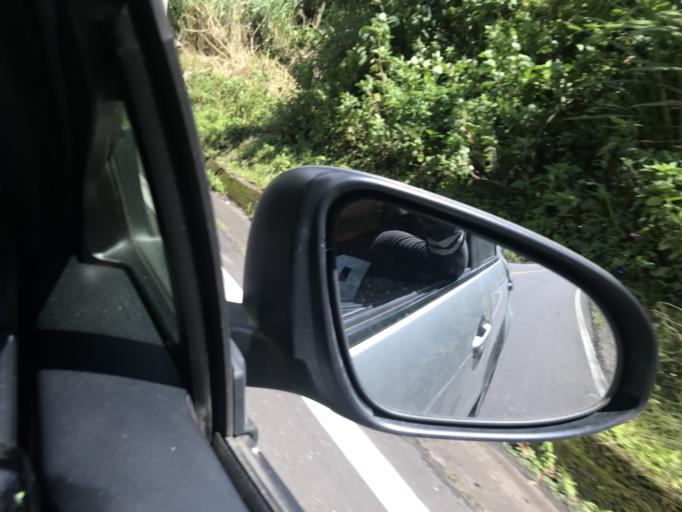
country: EC
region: Tungurahua
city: Banos
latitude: -1.4068
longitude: -78.4061
